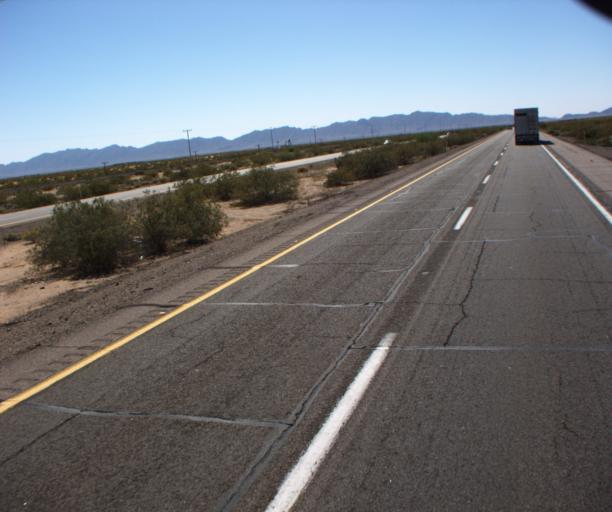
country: US
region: Arizona
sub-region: Yuma County
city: Wellton
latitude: 32.7814
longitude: -113.5816
